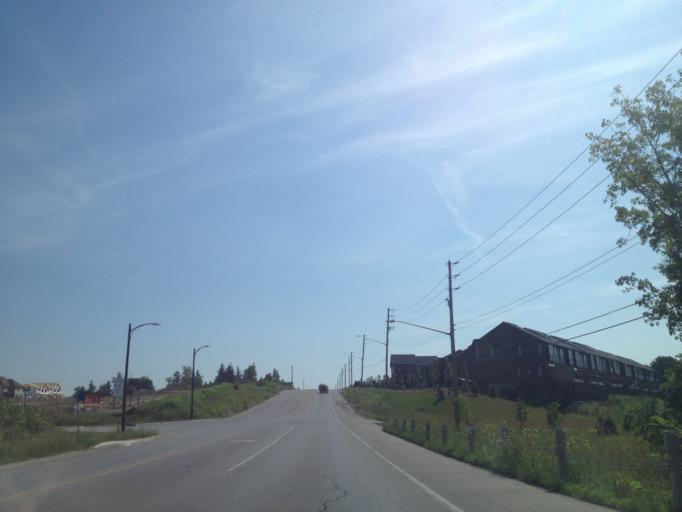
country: CA
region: Ontario
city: London
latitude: 43.0435
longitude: -81.2714
